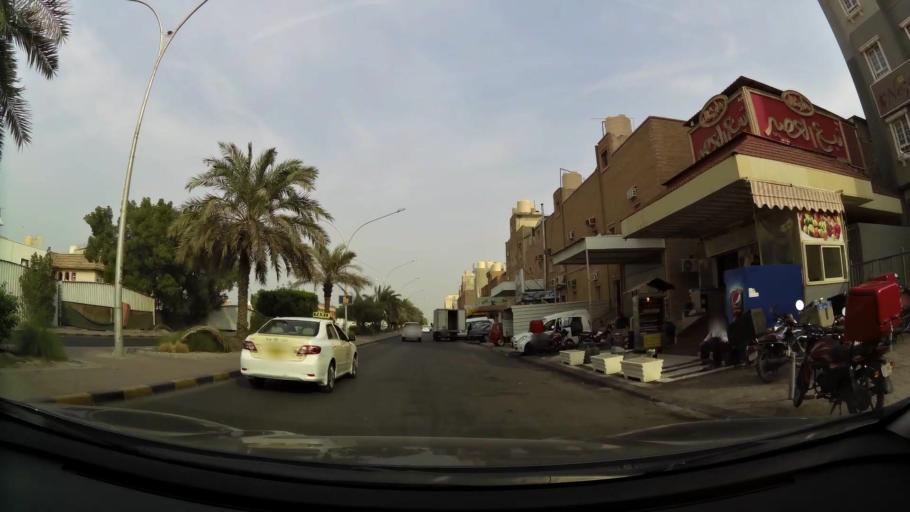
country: KW
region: Al Farwaniyah
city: Al Farwaniyah
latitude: 29.2973
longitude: 47.9708
